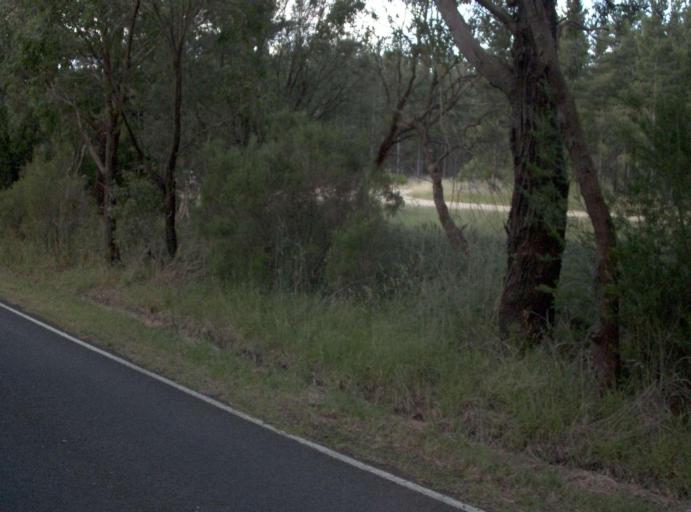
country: AU
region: Victoria
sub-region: Latrobe
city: Morwell
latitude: -38.2001
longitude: 146.4019
